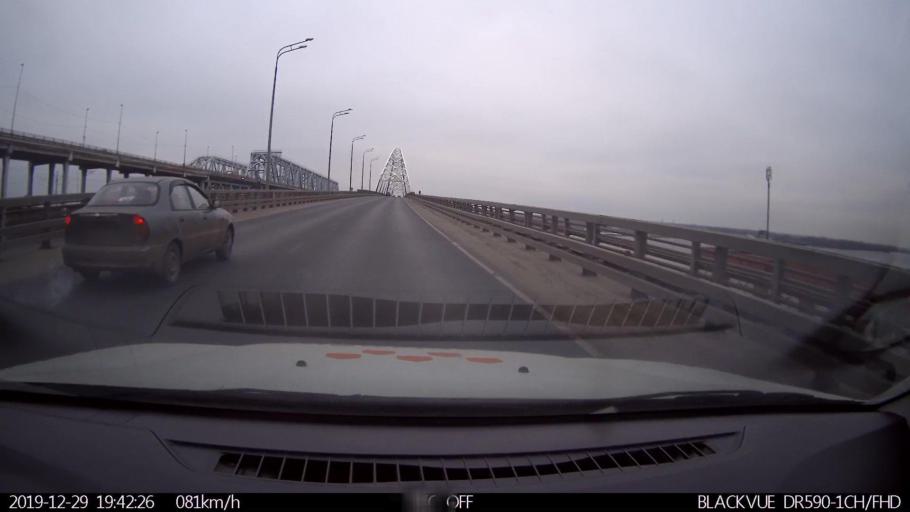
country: RU
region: Nizjnij Novgorod
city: Nizhniy Novgorod
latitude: 56.3499
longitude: 43.9238
